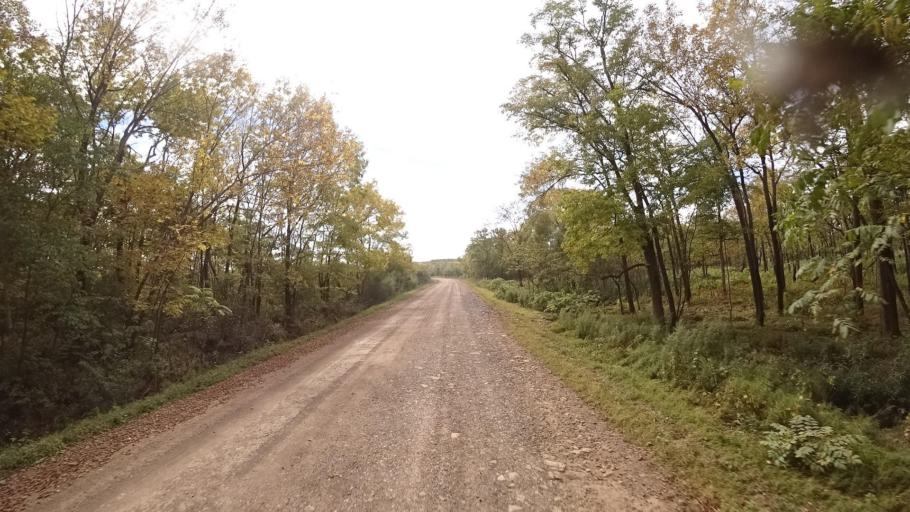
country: RU
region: Primorskiy
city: Yakovlevka
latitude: 44.5315
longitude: 133.6006
